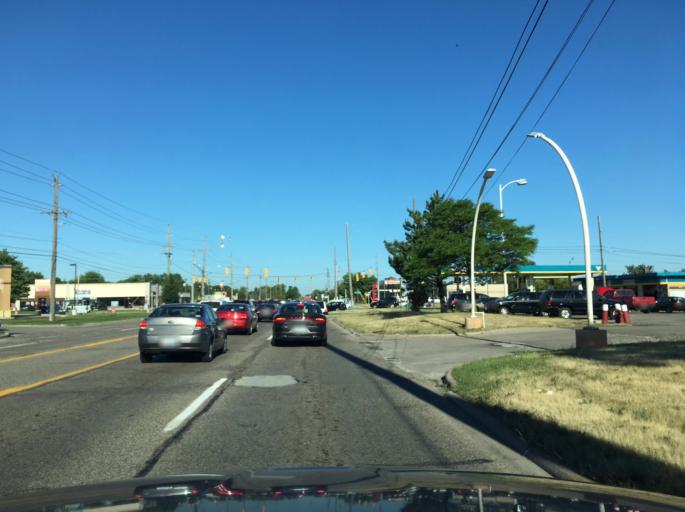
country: US
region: Michigan
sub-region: Macomb County
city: Fraser
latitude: 42.5380
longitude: -82.9876
